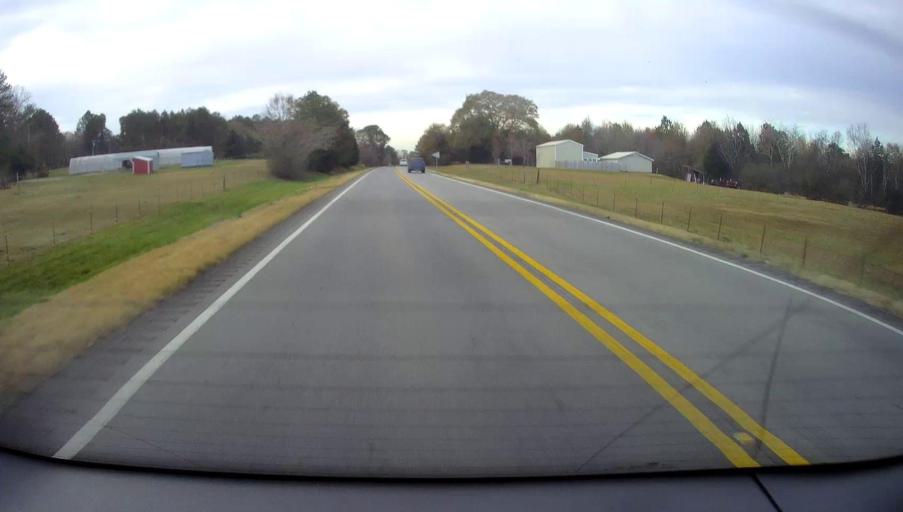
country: US
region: Alabama
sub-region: Marshall County
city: Arab
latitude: 34.3886
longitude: -86.6670
